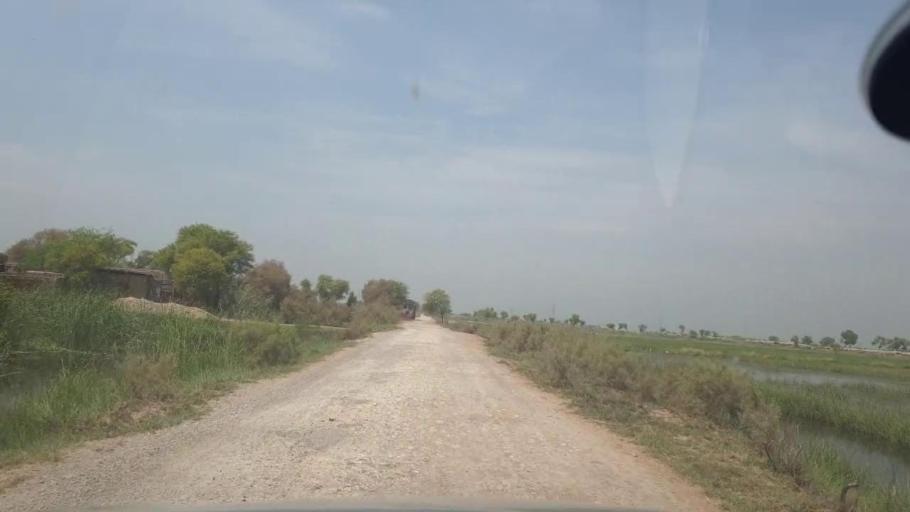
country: PK
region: Sindh
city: Thul
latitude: 28.1763
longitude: 68.6234
